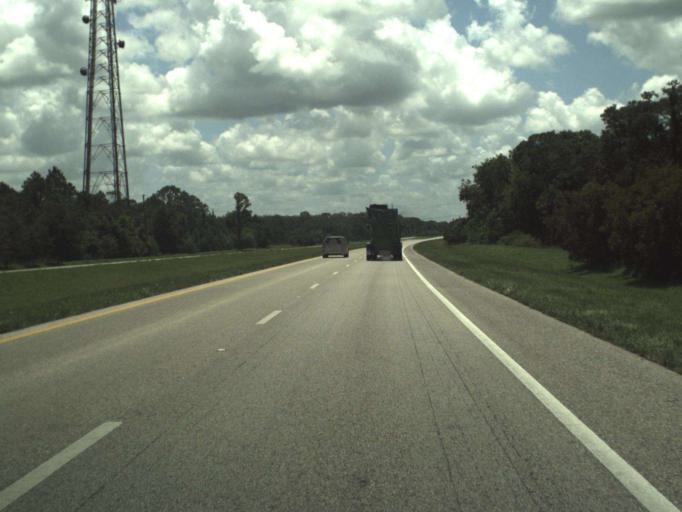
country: US
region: Florida
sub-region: Indian River County
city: Fellsmere
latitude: 27.6728
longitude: -80.8077
